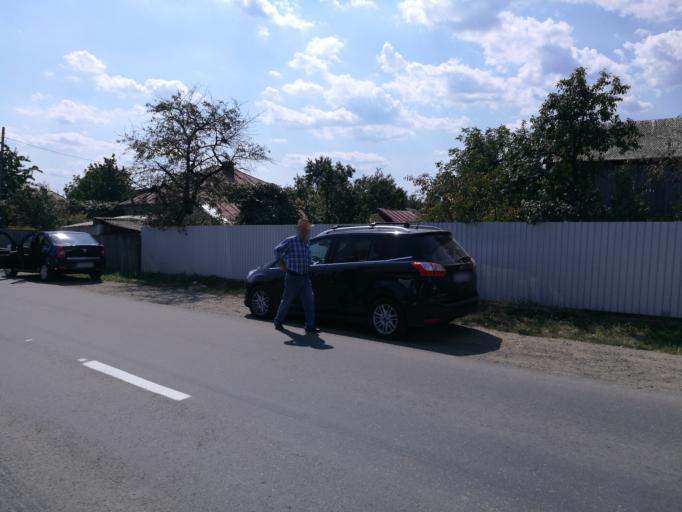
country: RO
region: Neamt
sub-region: Oras Targu Neamt
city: Humulesti
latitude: 47.1973
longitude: 26.3560
